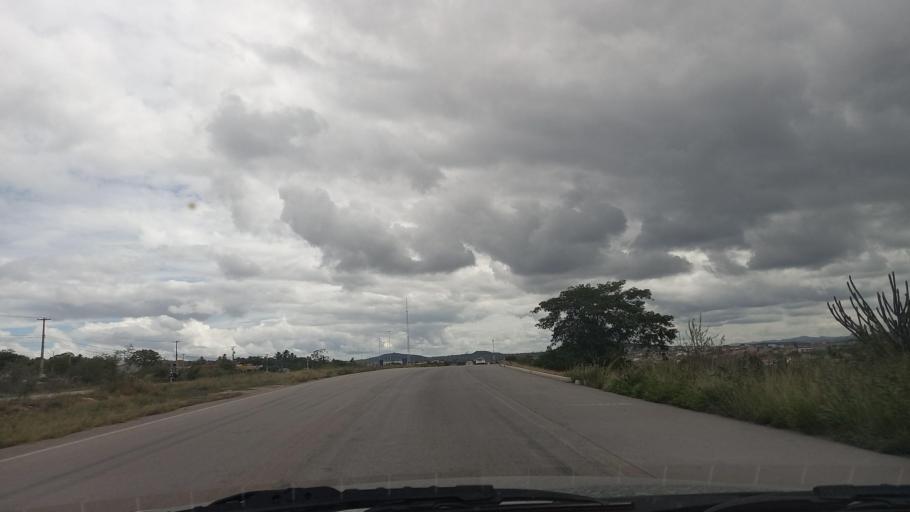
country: BR
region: Pernambuco
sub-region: Caruaru
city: Caruaru
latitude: -8.3284
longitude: -36.1198
